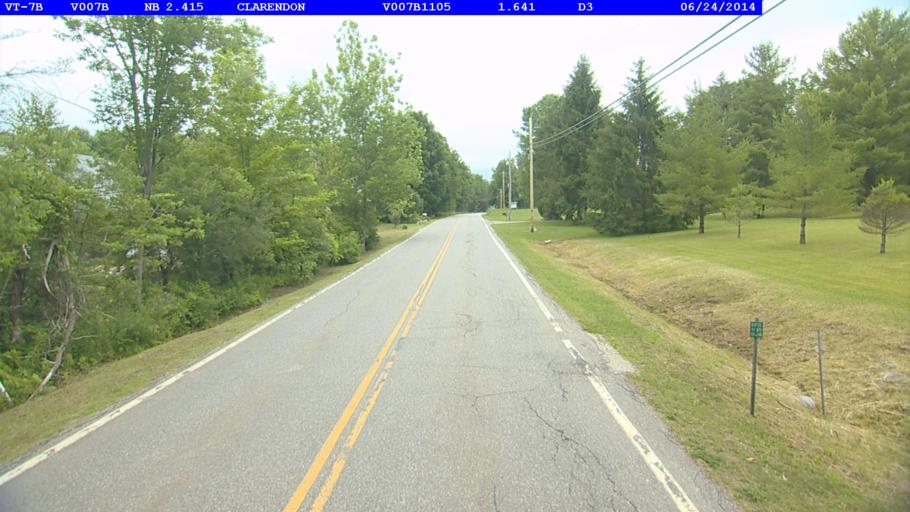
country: US
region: Vermont
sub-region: Rutland County
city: Rutland
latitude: 43.5246
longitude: -72.9599
